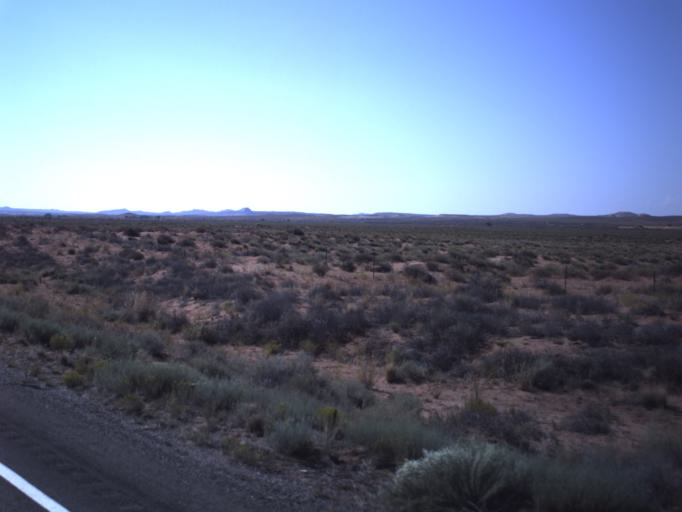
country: US
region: Utah
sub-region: San Juan County
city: Blanding
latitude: 37.1393
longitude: -109.5575
